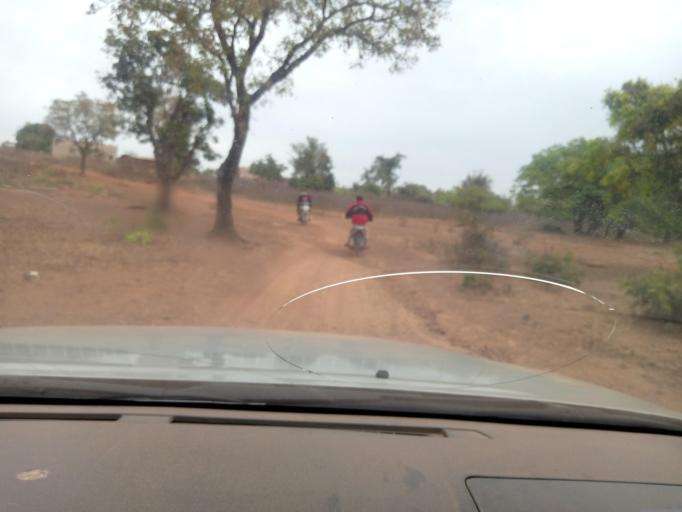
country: ML
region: Sikasso
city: Sikasso
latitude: 11.0190
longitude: -5.7141
